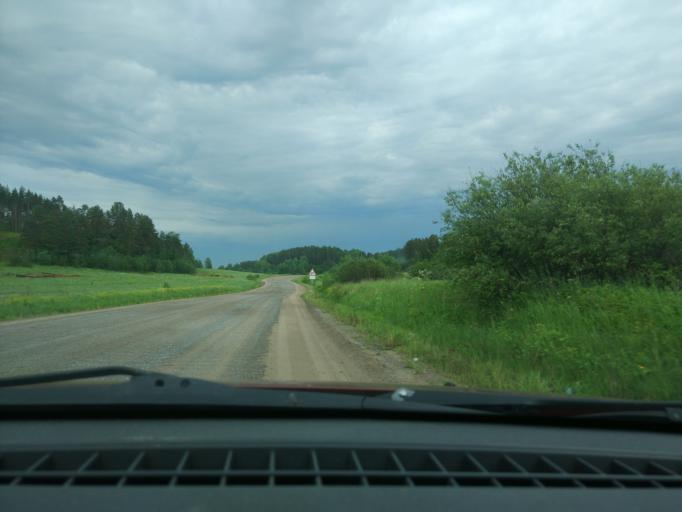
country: RU
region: Leningrad
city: Kuznechnoye
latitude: 61.2774
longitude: 29.8487
